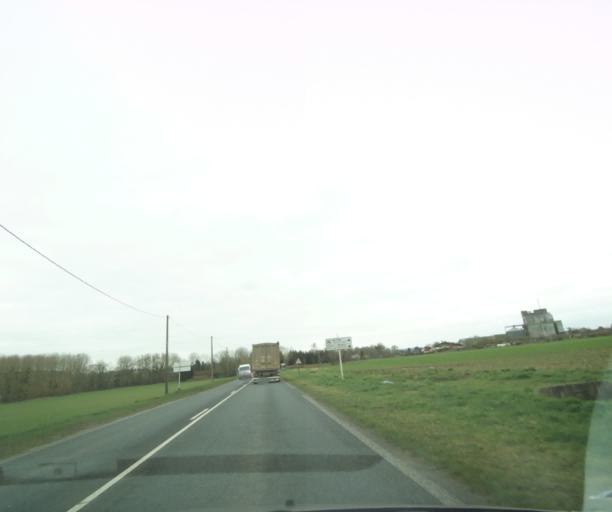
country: FR
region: Picardie
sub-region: Departement de l'Oise
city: Noyon
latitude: 49.5918
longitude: 2.9832
